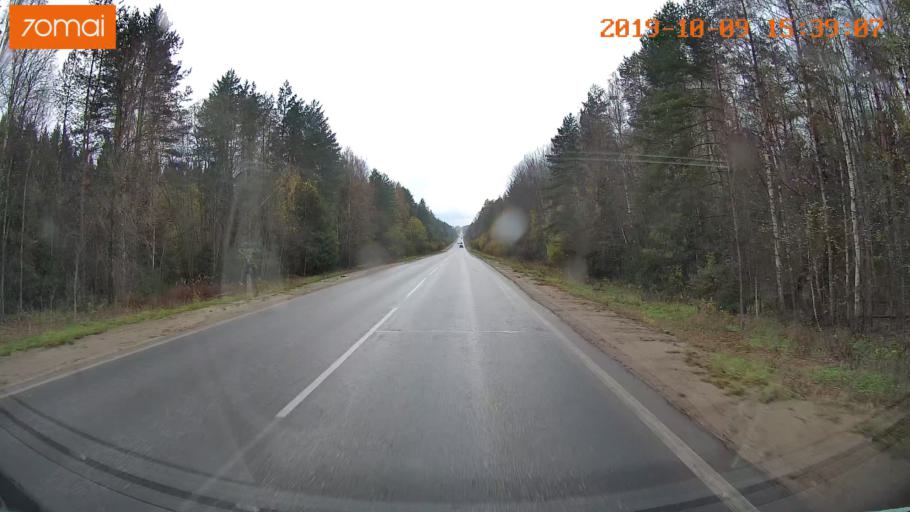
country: RU
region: Kostroma
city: Oktyabr'skiy
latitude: 57.9002
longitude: 41.1712
